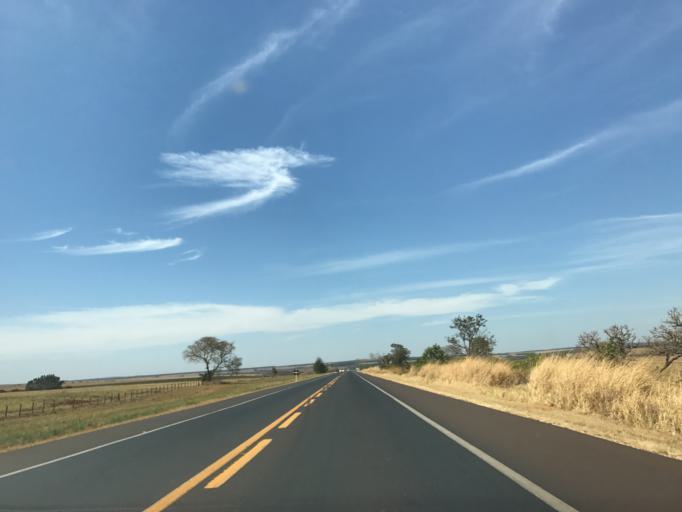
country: BR
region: Minas Gerais
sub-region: Monte Alegre De Minas
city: Monte Alegre de Minas
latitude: -19.0131
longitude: -49.0168
